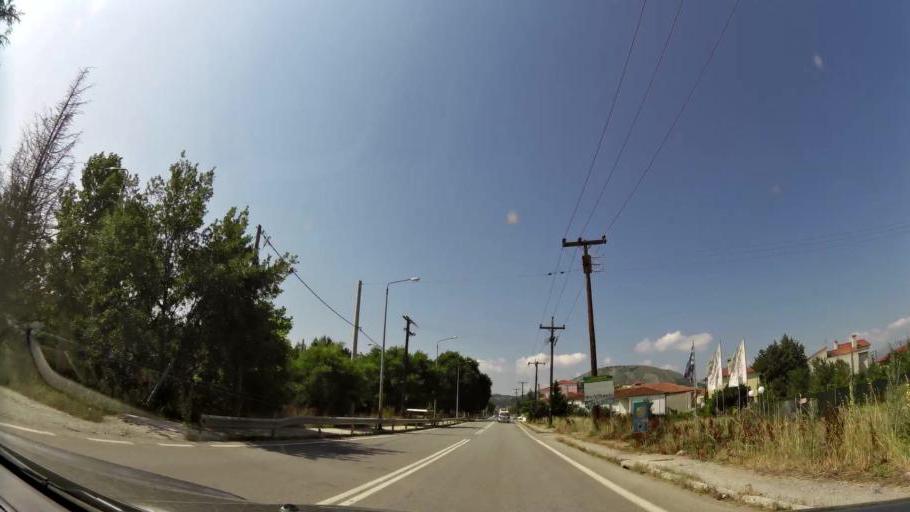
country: GR
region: West Macedonia
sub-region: Nomos Kozanis
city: Koila
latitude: 40.3336
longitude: 21.7908
